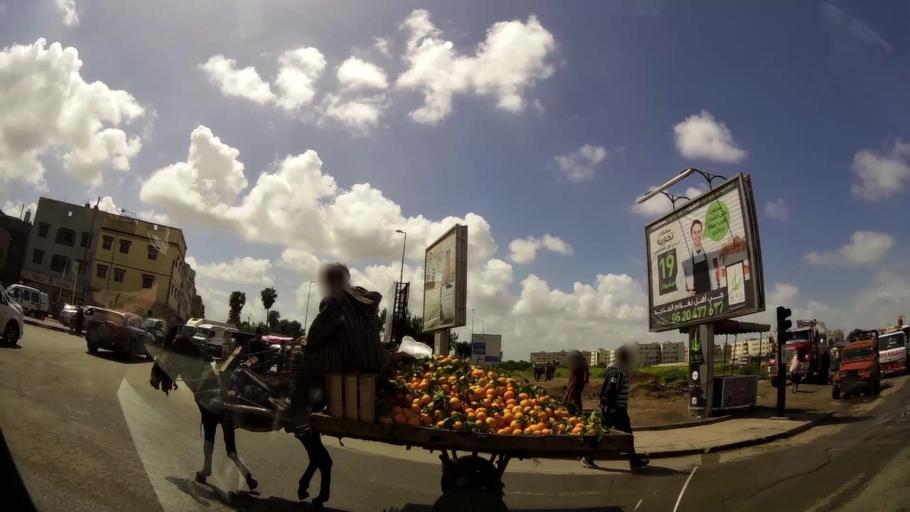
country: MA
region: Grand Casablanca
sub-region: Mediouna
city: Tit Mellil
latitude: 33.6348
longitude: -7.4512
